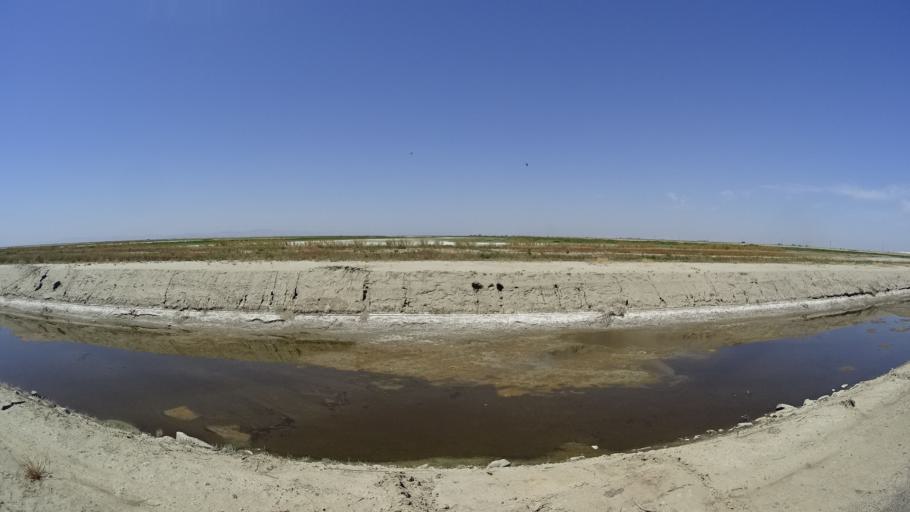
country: US
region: California
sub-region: Kings County
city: Corcoran
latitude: 36.1334
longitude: -119.6802
